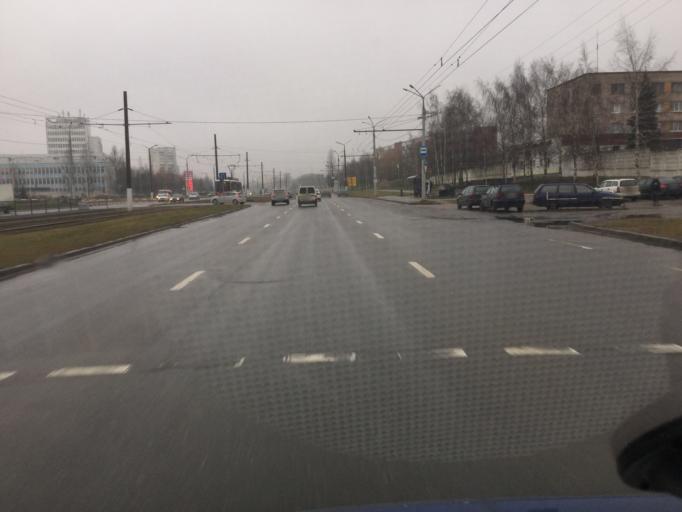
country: BY
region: Vitebsk
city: Vitebsk
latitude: 55.1632
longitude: 30.2384
